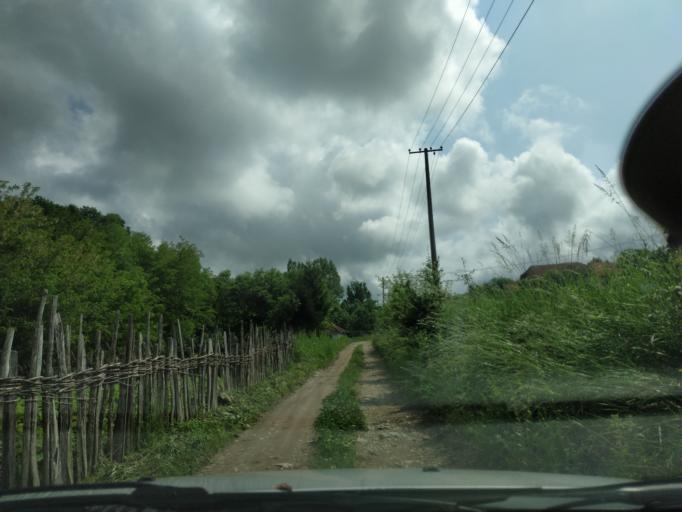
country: RS
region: Central Serbia
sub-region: Nisavski Okrug
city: Aleksinac
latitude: 43.4252
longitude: 21.5857
